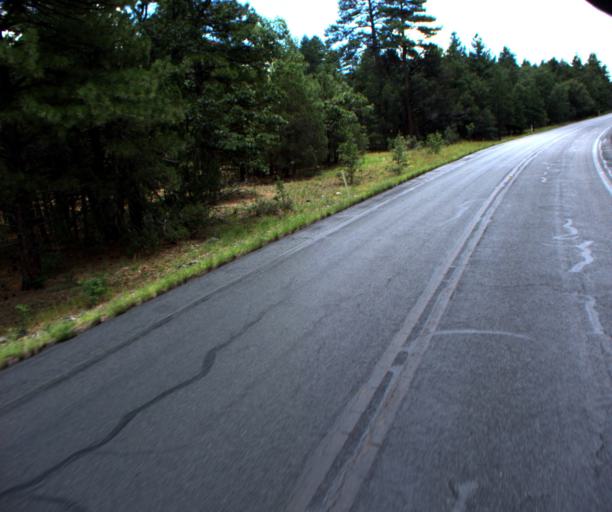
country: US
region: Arizona
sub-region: Gila County
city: Pine
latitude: 34.5201
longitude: -111.5074
